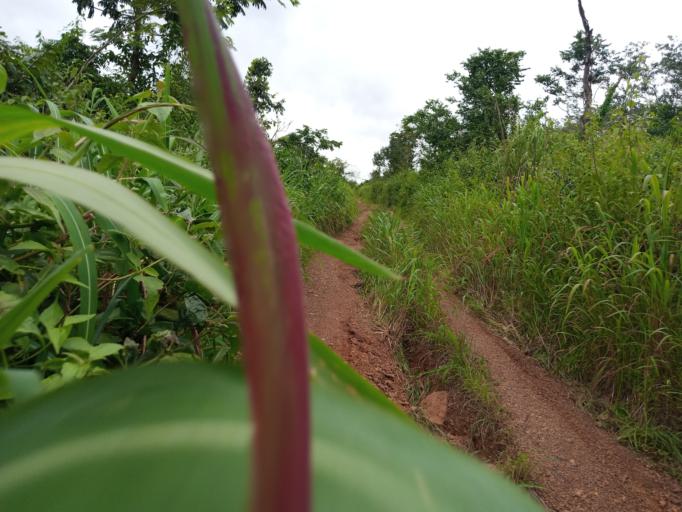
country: SL
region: Southern Province
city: Largo
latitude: 8.1995
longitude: -12.0529
